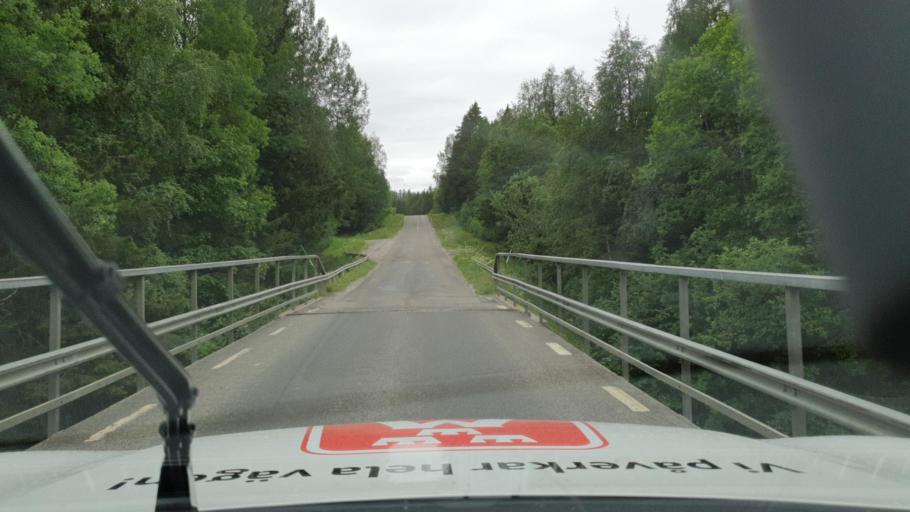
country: SE
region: Vaesterbotten
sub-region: Bjurholms Kommun
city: Bjurholm
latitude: 63.7955
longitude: 19.3465
